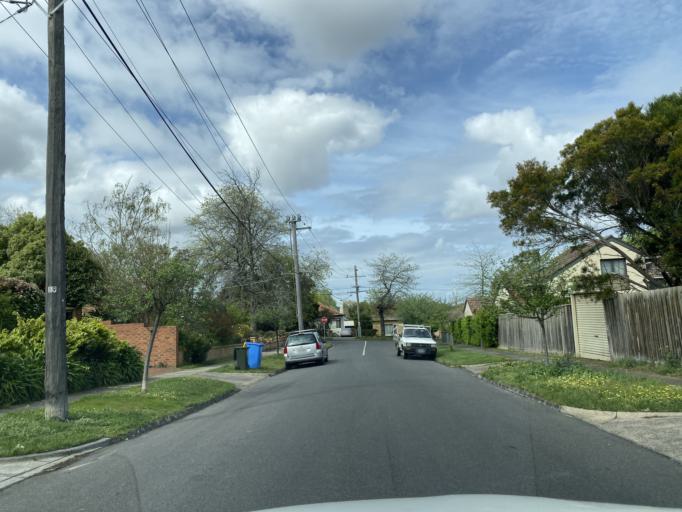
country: AU
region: Victoria
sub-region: Boroondara
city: Ashburton
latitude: -37.8543
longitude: 145.0851
